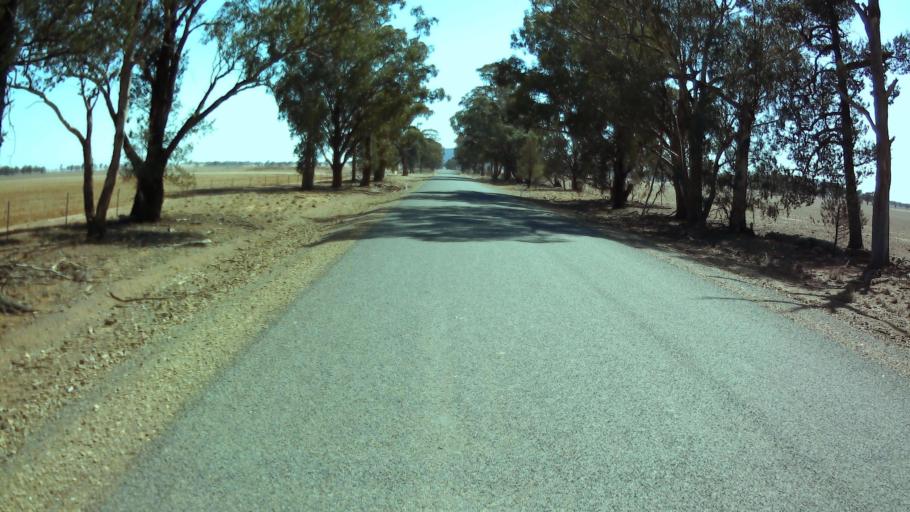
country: AU
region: New South Wales
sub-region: Weddin
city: Grenfell
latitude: -33.7175
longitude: 147.9037
